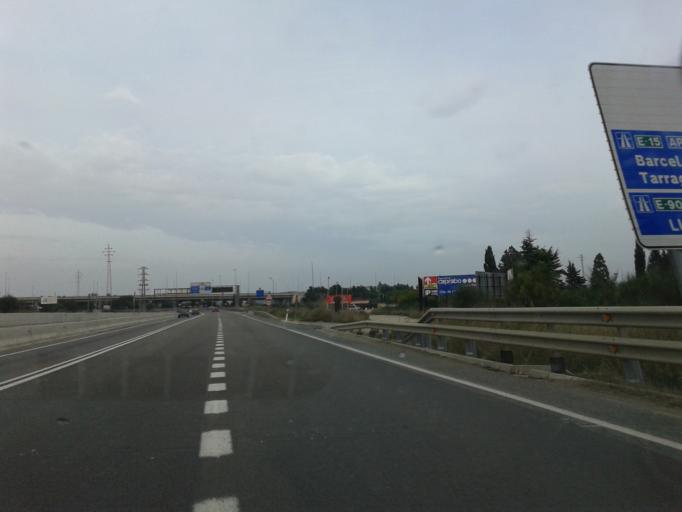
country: ES
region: Catalonia
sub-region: Provincia de Tarragona
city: El Vendrell
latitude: 41.1920
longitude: 1.5231
